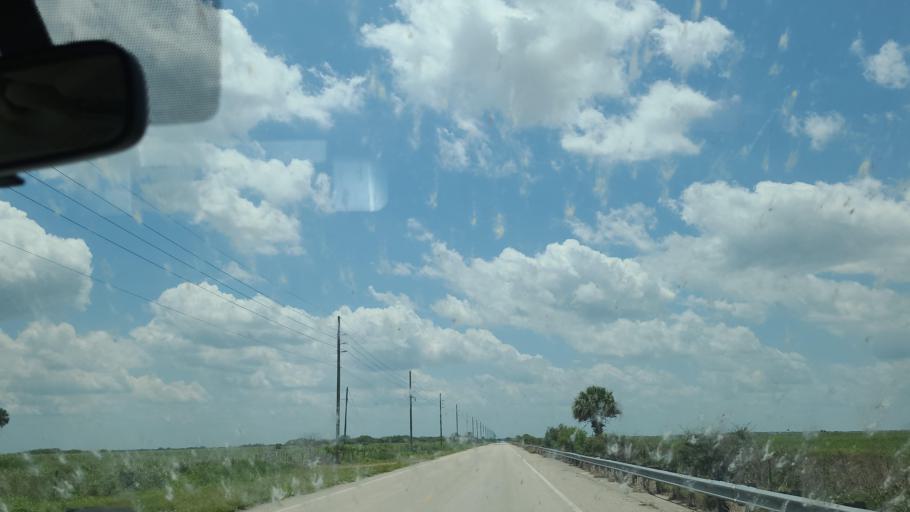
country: US
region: Florida
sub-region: Glades County
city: Buckhead Ridge
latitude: 27.1866
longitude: -81.0944
